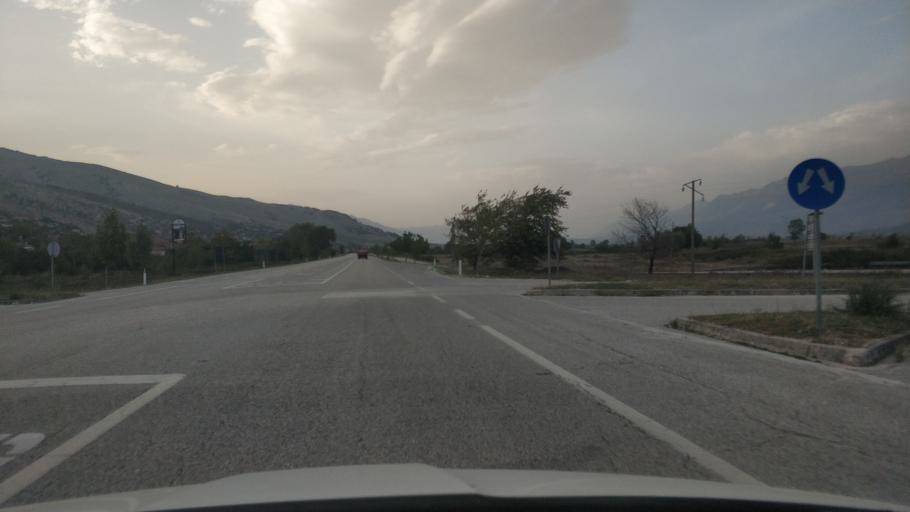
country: AL
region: Gjirokaster
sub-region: Rrethi i Gjirokastres
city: Libohove
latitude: 39.9521
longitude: 20.2543
